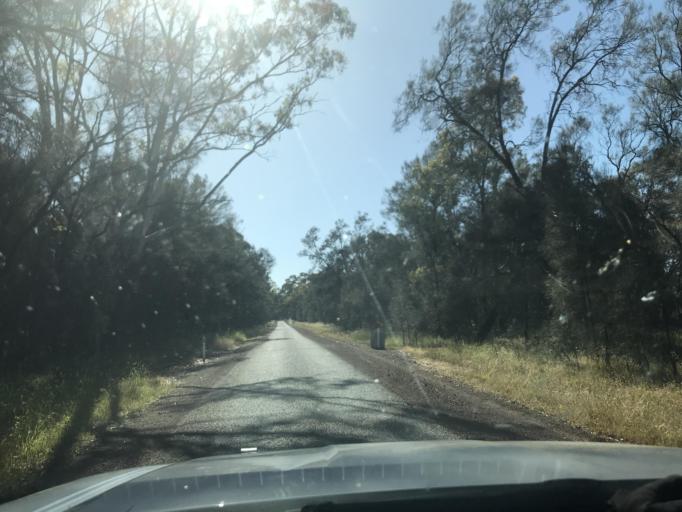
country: AU
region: Victoria
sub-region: Horsham
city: Horsham
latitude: -37.0119
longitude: 141.6662
